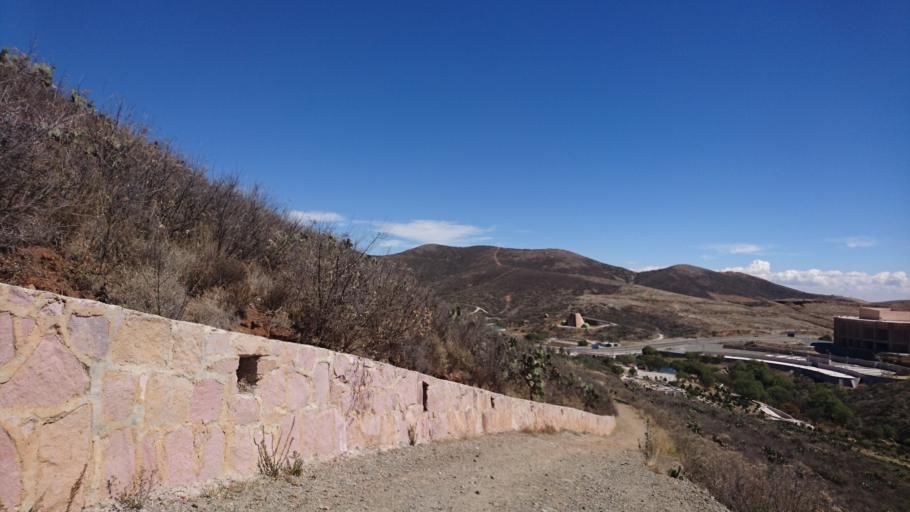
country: MX
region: Zacatecas
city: Zacatecas
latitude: 22.7789
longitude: -102.5481
